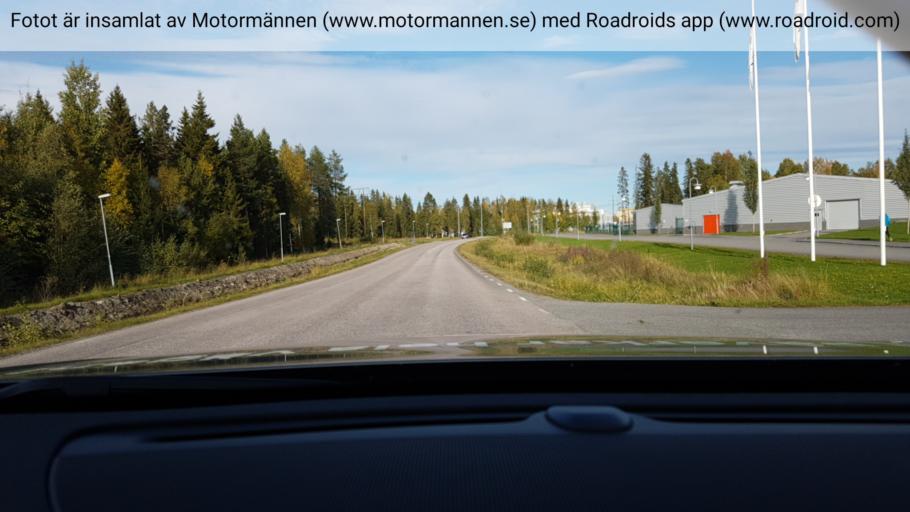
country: SE
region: Norrbotten
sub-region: Lulea Kommun
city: Bergnaset
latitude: 65.6132
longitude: 22.1187
